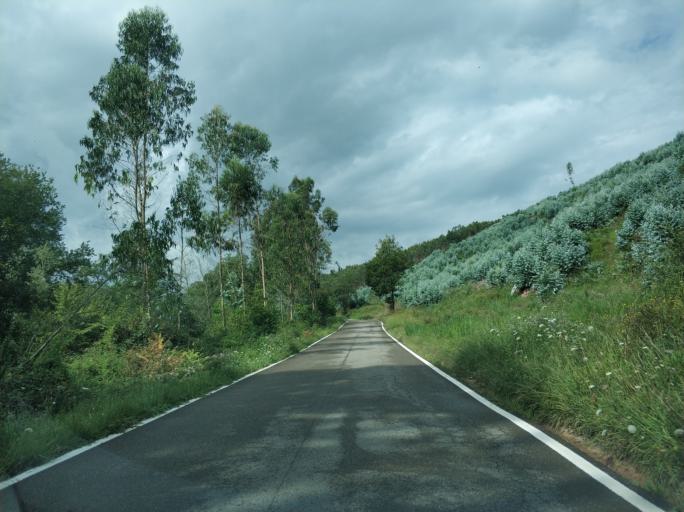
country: ES
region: Cantabria
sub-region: Provincia de Cantabria
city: Miengo
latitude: 43.3935
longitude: -3.9581
